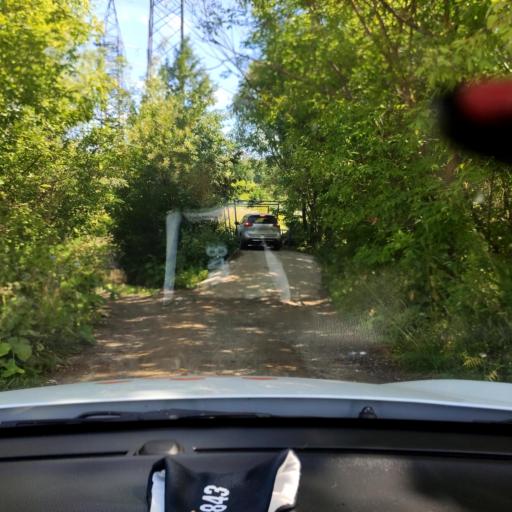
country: RU
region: Tatarstan
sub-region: Gorod Kazan'
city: Kazan
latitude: 55.8244
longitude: 49.2046
